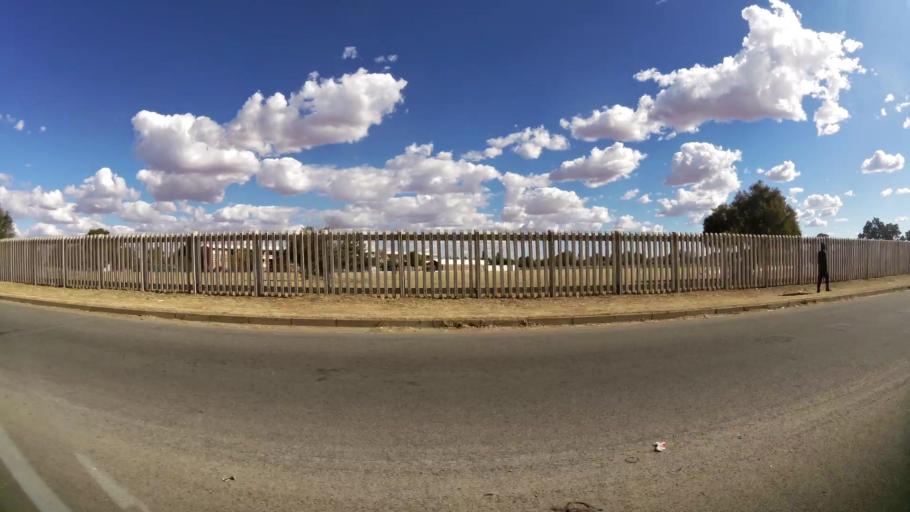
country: ZA
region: North-West
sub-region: Dr Kenneth Kaunda District Municipality
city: Klerksdorp
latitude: -26.8590
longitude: 26.6457
